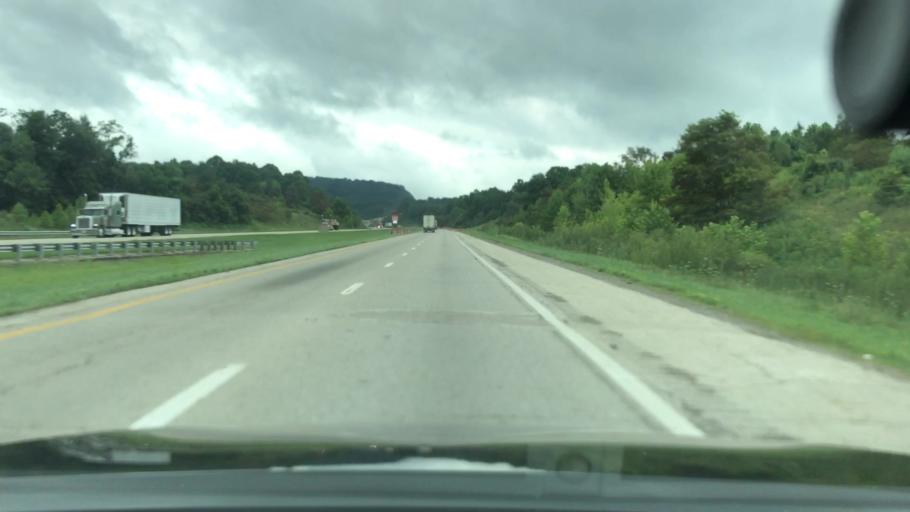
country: US
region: Ohio
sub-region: Ross County
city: Chillicothe
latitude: 39.2489
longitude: -82.8486
